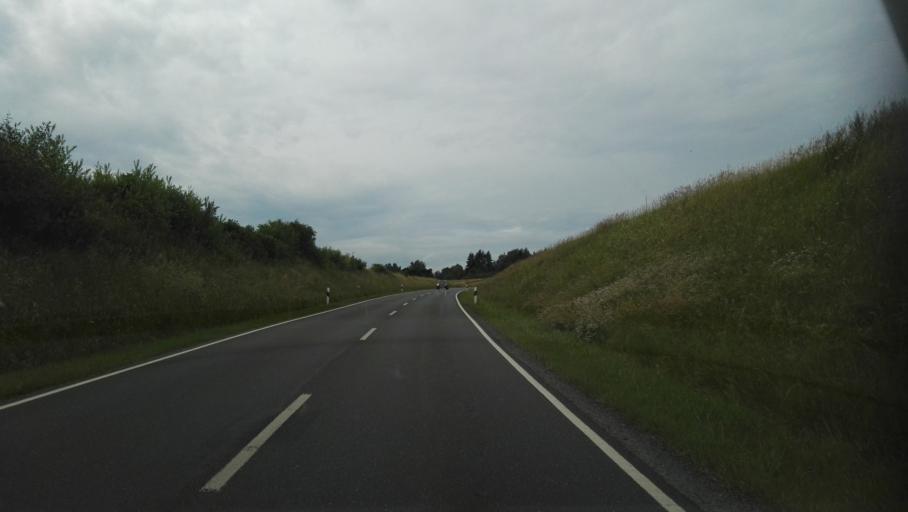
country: DE
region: Bavaria
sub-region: Upper Franconia
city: Hollfeld
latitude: 49.9200
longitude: 11.3077
